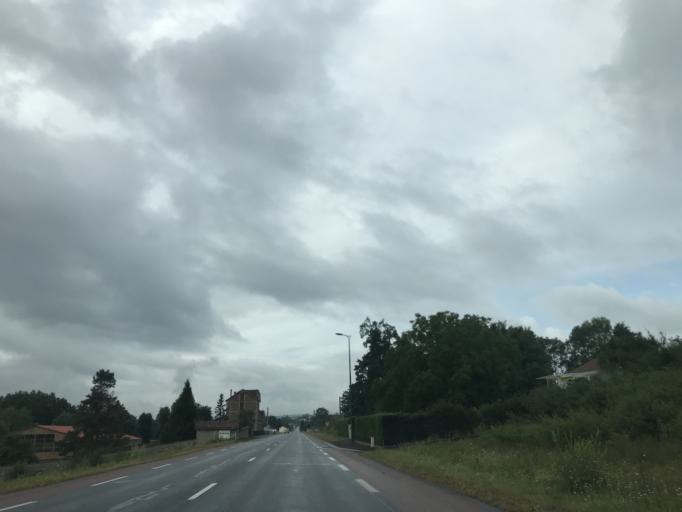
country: FR
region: Auvergne
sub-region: Departement du Puy-de-Dome
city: Arlanc
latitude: 45.4335
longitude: 3.7242
